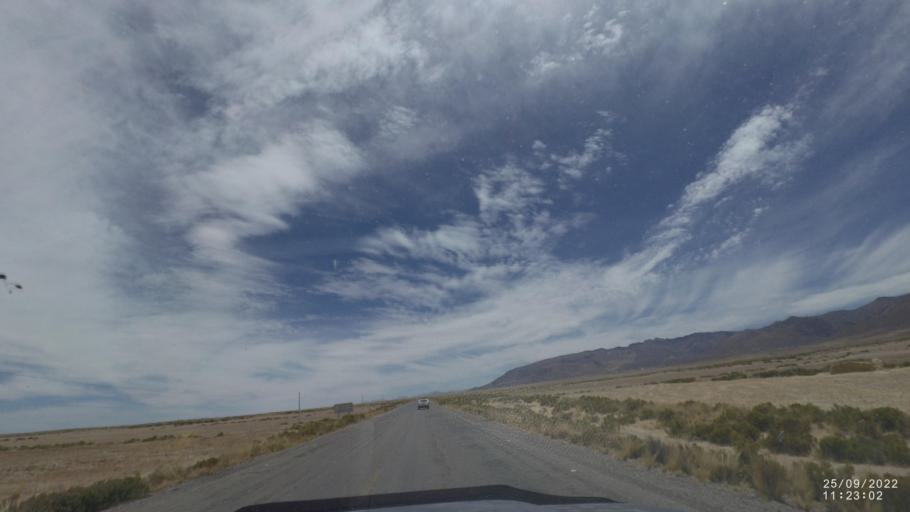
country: BO
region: Oruro
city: Challapata
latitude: -19.1164
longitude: -66.7698
